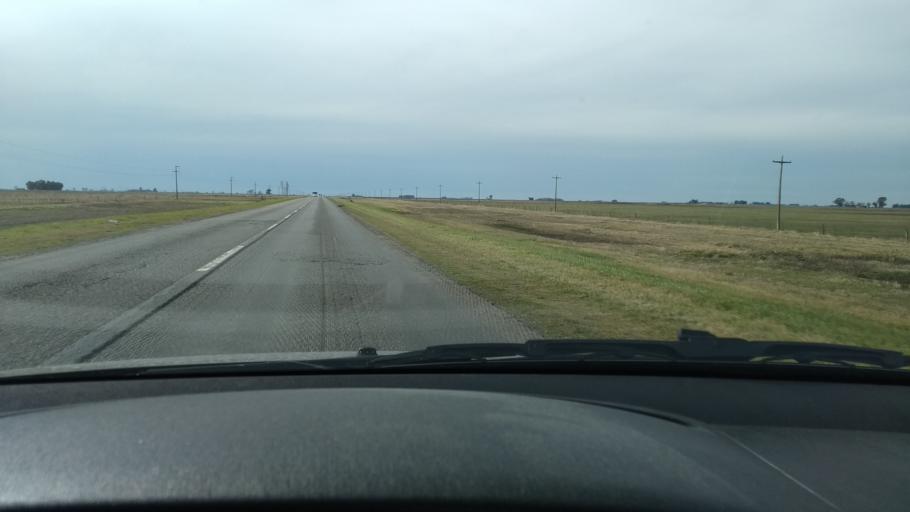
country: AR
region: Buenos Aires
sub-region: Partido de Azul
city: Azul
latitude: -36.6916
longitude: -59.7396
